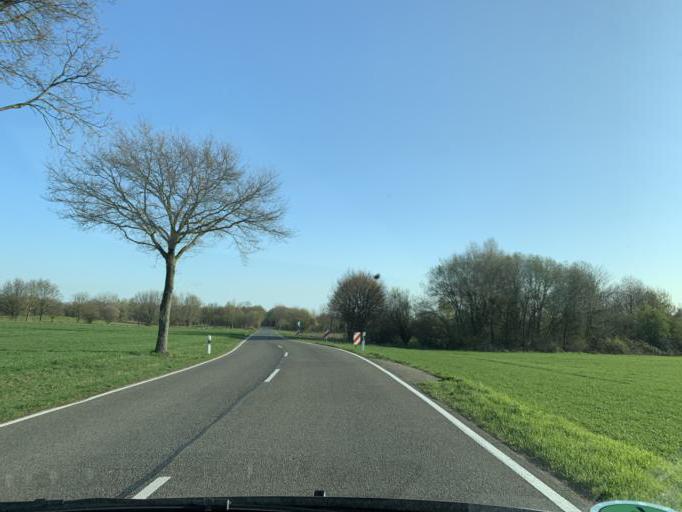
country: DE
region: North Rhine-Westphalia
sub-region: Regierungsbezirk Koln
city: Titz
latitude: 51.0877
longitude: 6.4025
